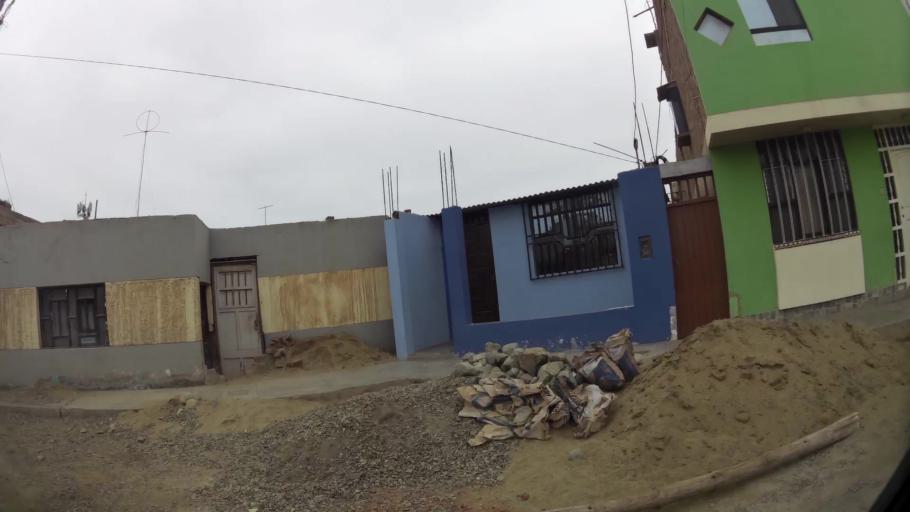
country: PE
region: La Libertad
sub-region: Provincia de Trujillo
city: Buenos Aires
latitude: -8.1409
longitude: -79.0483
